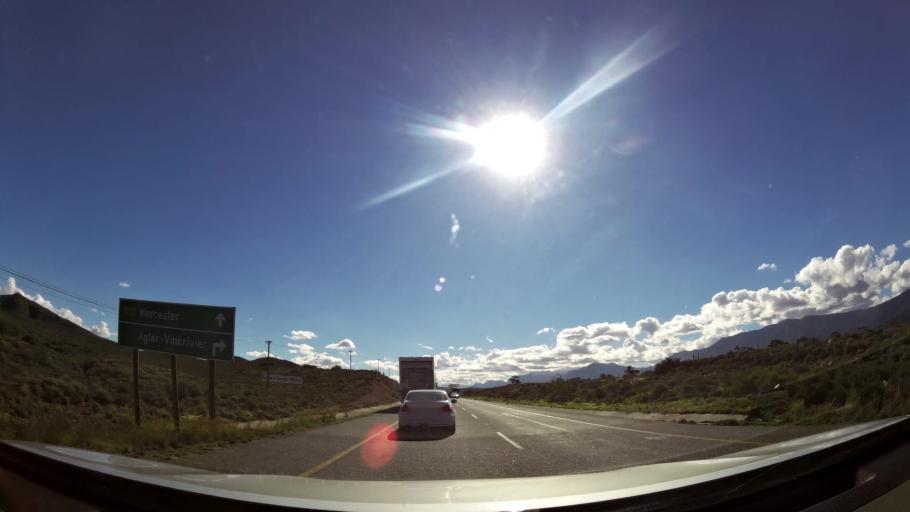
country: ZA
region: Western Cape
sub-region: Cape Winelands District Municipality
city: Worcester
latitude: -33.7644
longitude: 19.7428
